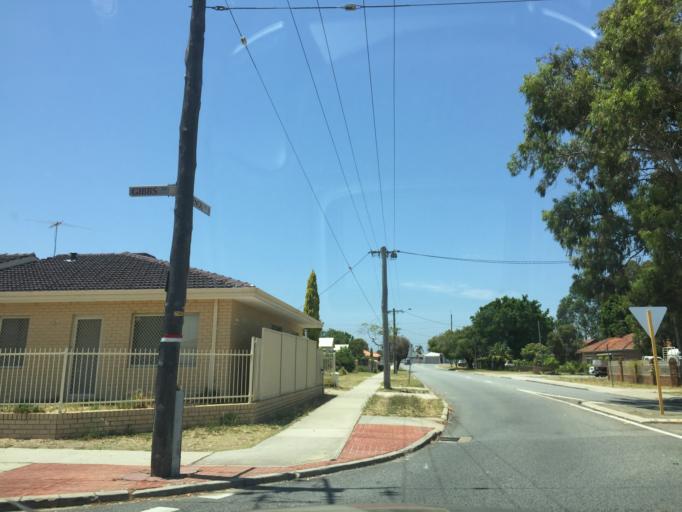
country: AU
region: Western Australia
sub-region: Canning
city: Cannington
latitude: -32.0125
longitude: 115.9474
